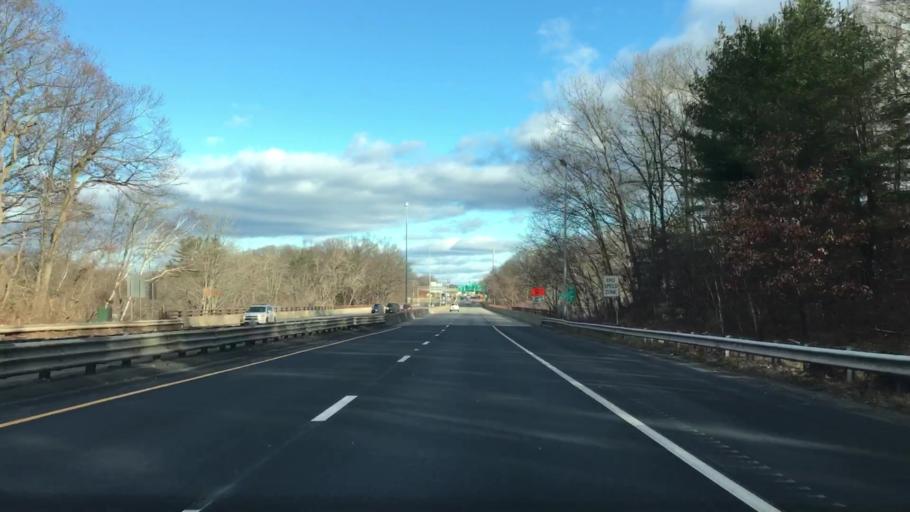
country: US
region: Massachusetts
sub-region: Hampden County
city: North Chicopee
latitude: 42.1560
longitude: -72.5485
